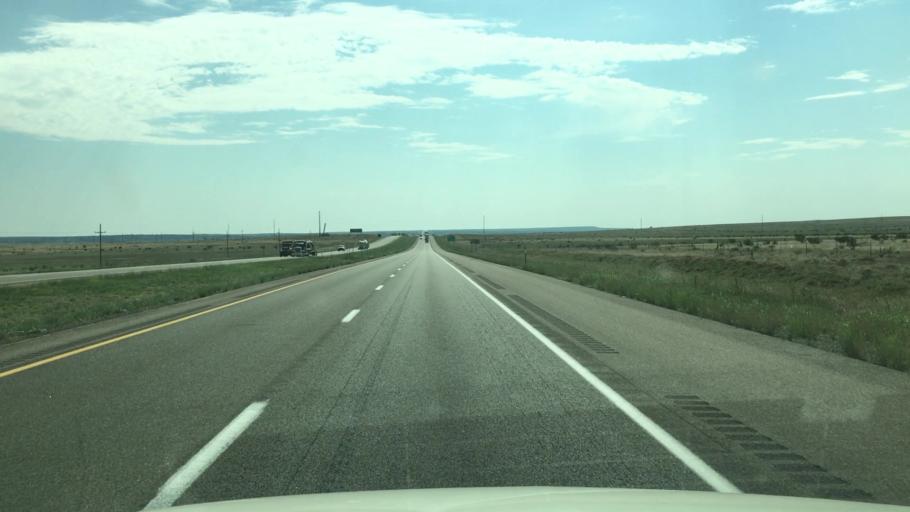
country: US
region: New Mexico
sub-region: Guadalupe County
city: Santa Rosa
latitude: 34.9785
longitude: -105.0344
